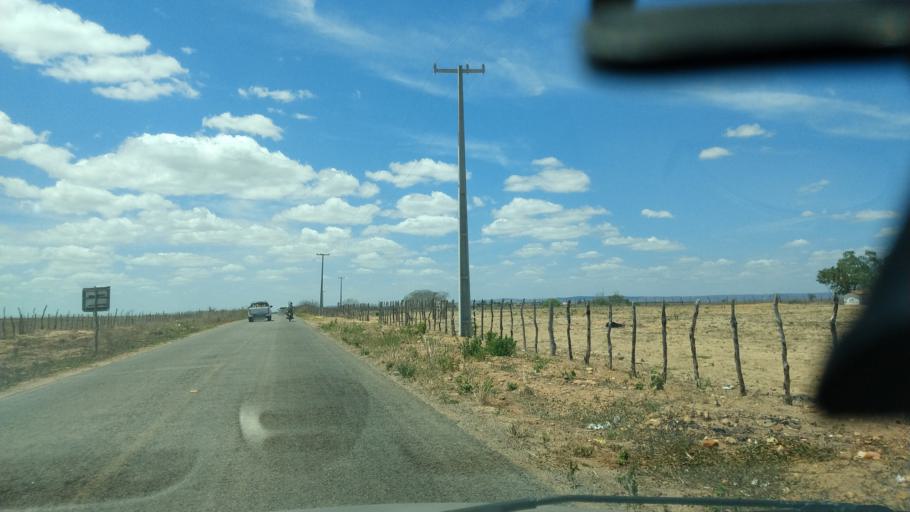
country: BR
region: Rio Grande do Norte
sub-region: Sao Paulo Do Potengi
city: Sao Paulo do Potengi
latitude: -5.9146
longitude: -35.7415
